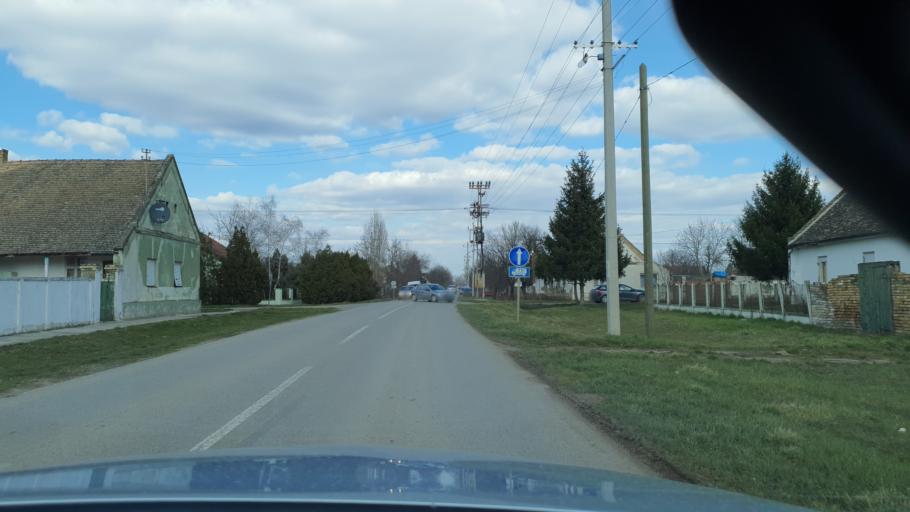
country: RS
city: Ravno Selo
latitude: 45.4484
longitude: 19.6097
